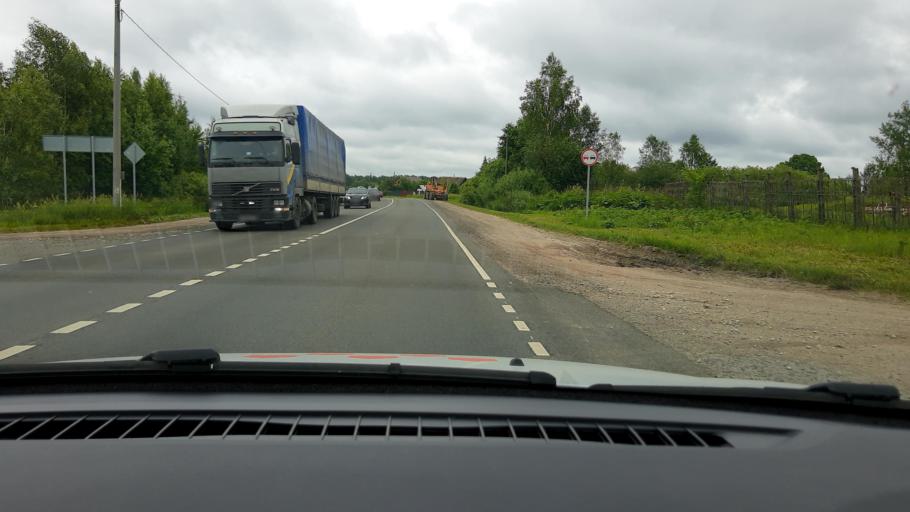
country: RU
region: Nizjnij Novgorod
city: Linda
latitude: 56.5992
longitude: 44.0420
